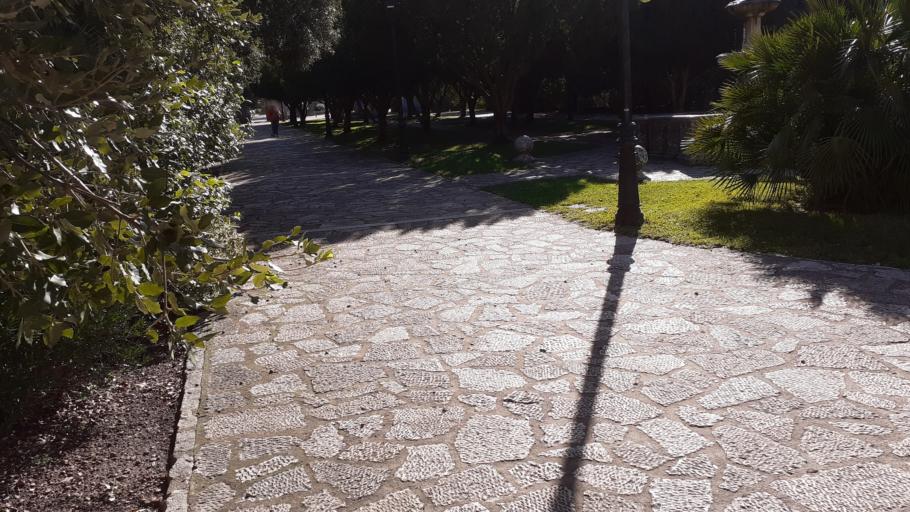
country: ES
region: Balearic Islands
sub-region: Illes Balears
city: Escorca
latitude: 39.8231
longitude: 2.8836
